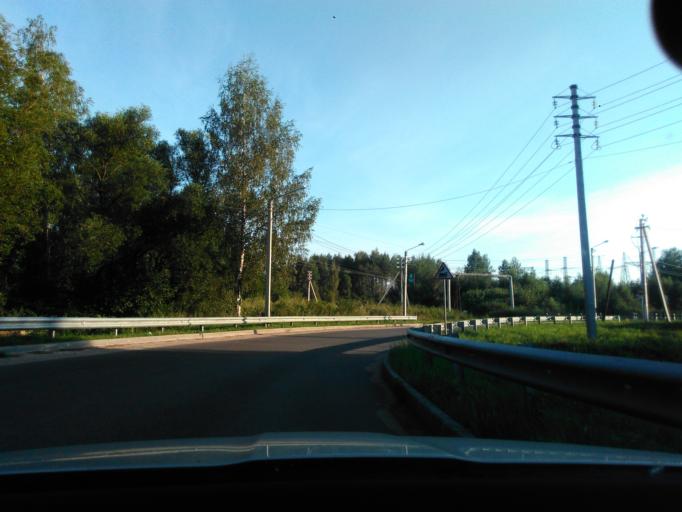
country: RU
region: Tverskaya
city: Konakovo
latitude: 56.7305
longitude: 36.7849
